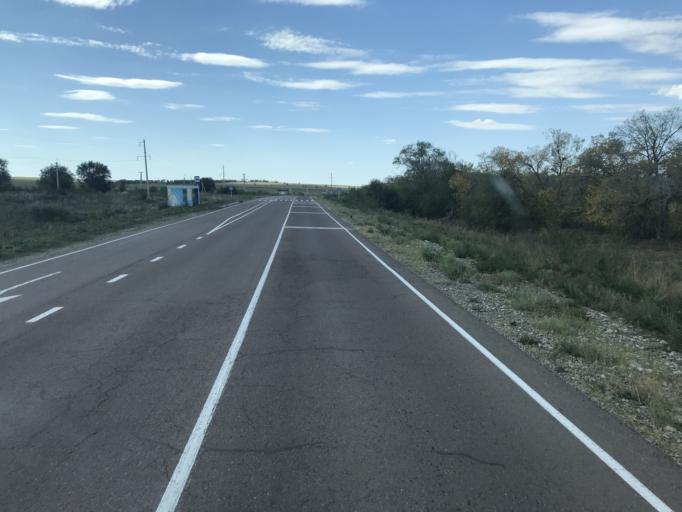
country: KZ
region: East Kazakhstan
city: Urzhar
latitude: 47.1057
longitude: 81.2719
